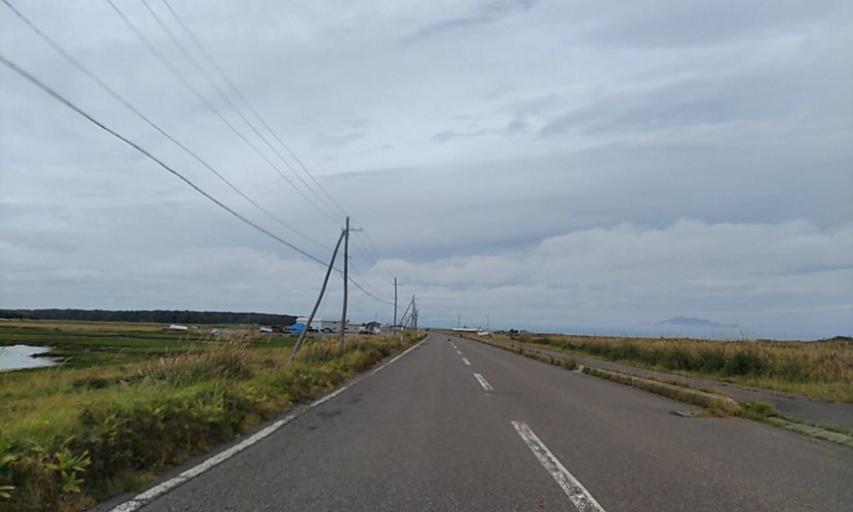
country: JP
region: Hokkaido
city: Shibetsu
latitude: 43.6035
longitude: 145.3010
